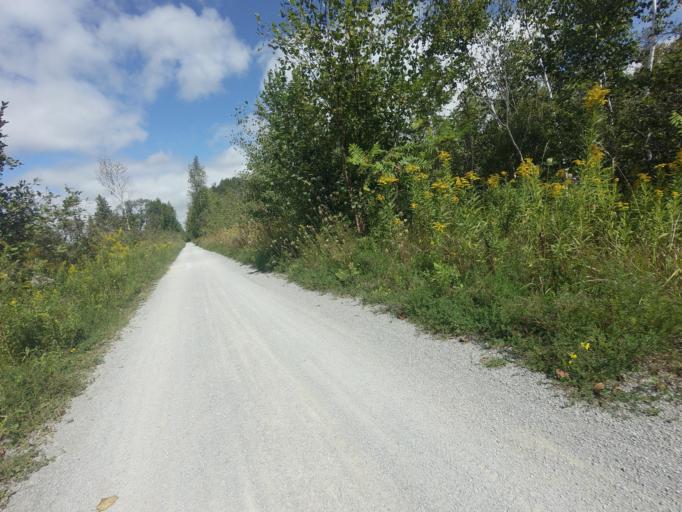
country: CA
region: Ontario
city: Uxbridge
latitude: 44.1458
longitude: -79.0859
